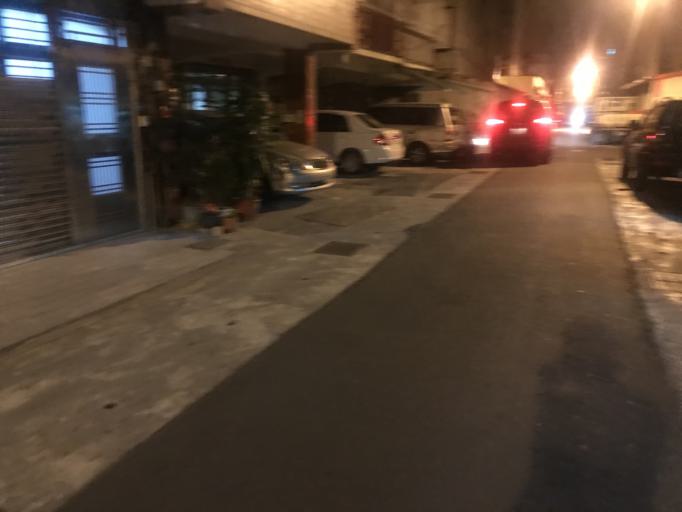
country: TW
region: Taiwan
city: Fengshan
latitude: 22.6329
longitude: 120.3348
